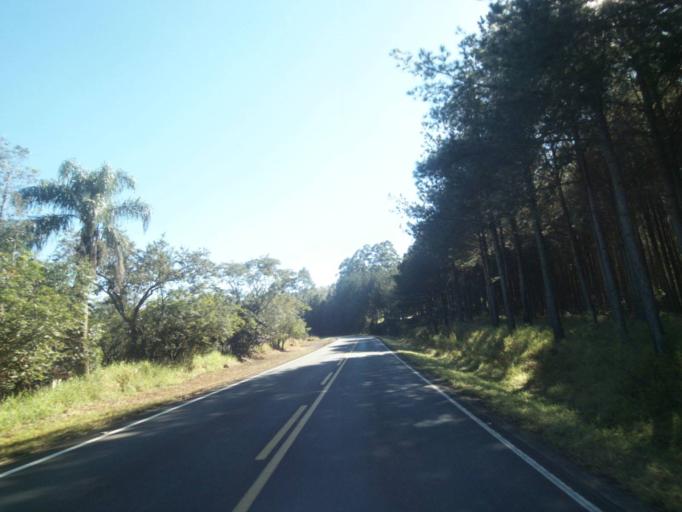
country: BR
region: Parana
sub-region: Telemaco Borba
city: Telemaco Borba
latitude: -24.4385
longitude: -50.5505
